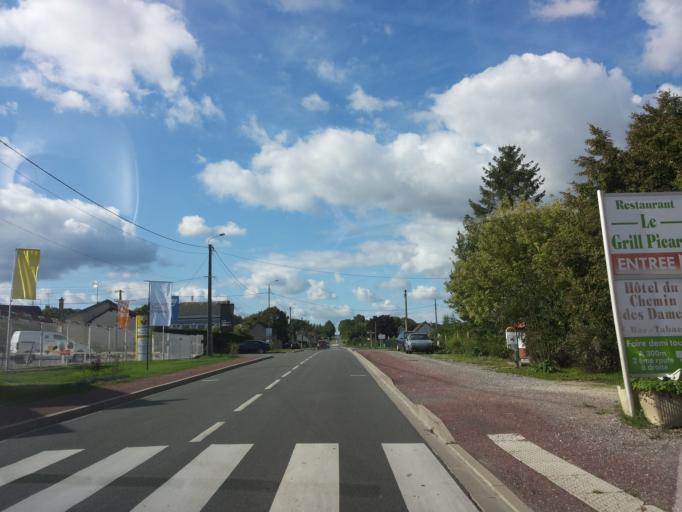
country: FR
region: Picardie
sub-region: Departement de l'Aisne
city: Saint-Erme-Outre-et-Ramecourt
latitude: 49.4650
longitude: 3.8210
